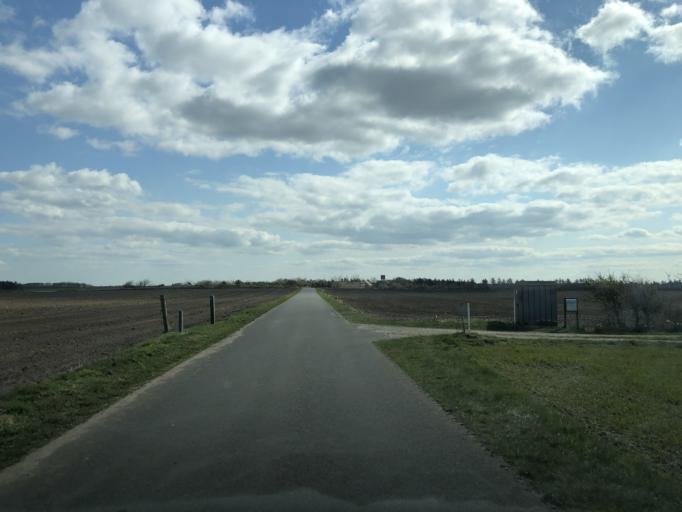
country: DK
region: Central Jutland
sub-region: Holstebro Kommune
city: Ulfborg
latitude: 56.4007
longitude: 8.2116
